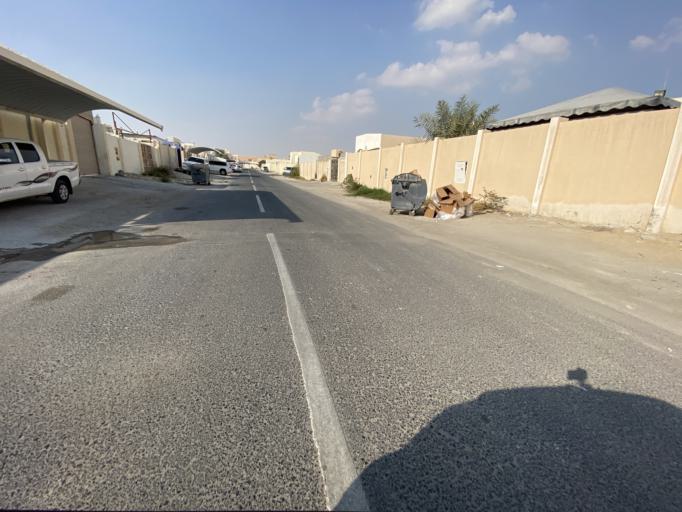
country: QA
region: Baladiyat ar Rayyan
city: Ar Rayyan
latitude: 25.2336
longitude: 51.3778
